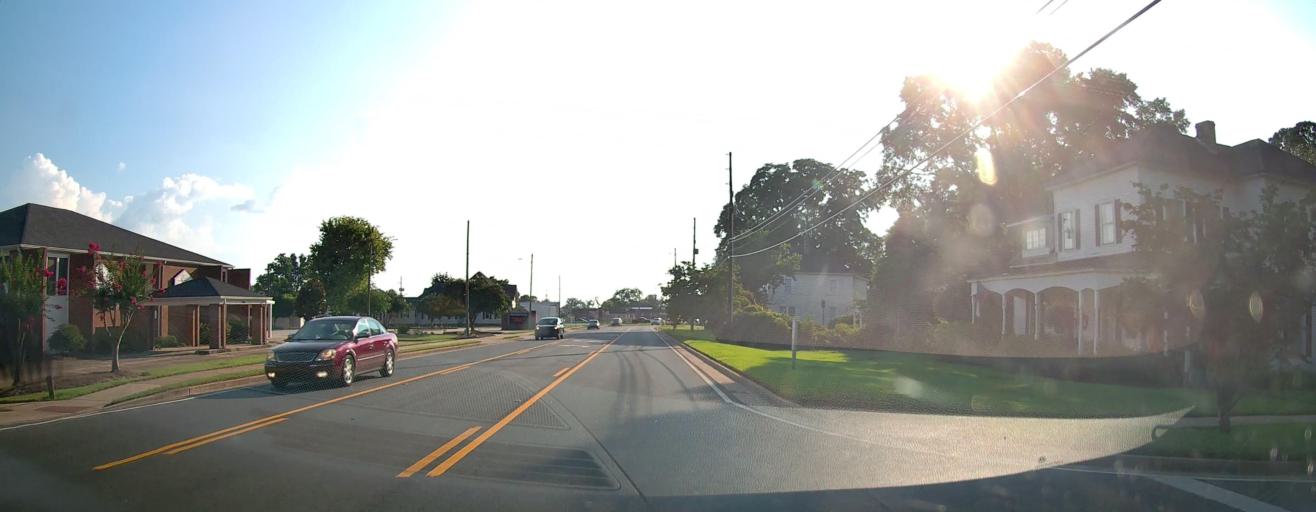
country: US
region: Georgia
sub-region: Houston County
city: Perry
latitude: 32.4612
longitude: -83.7284
